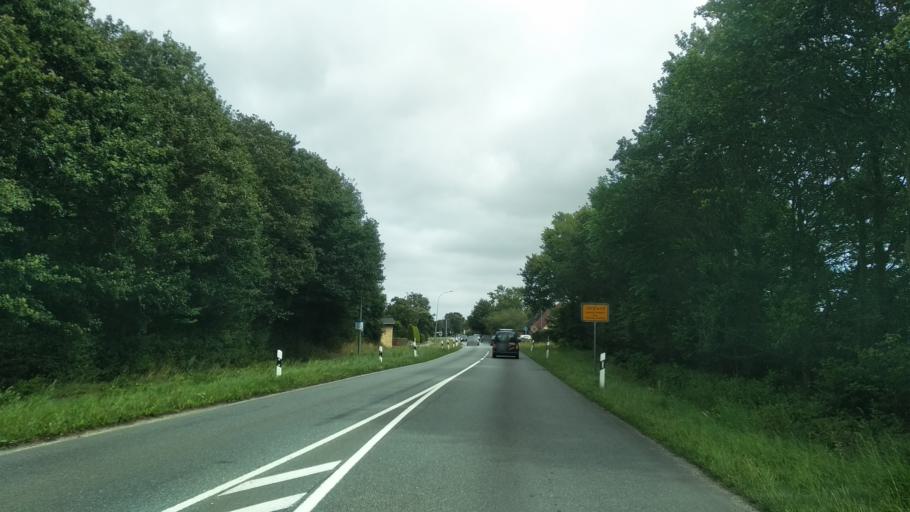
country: DE
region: Schleswig-Holstein
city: Jarplund-Weding
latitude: 54.7399
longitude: 9.4293
